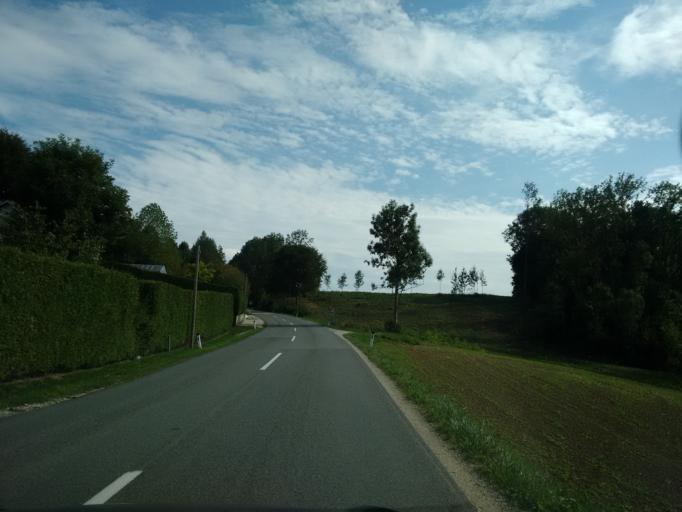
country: AT
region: Upper Austria
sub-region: Wels-Land
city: Thalheim bei Wels
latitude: 48.1407
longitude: 14.0497
